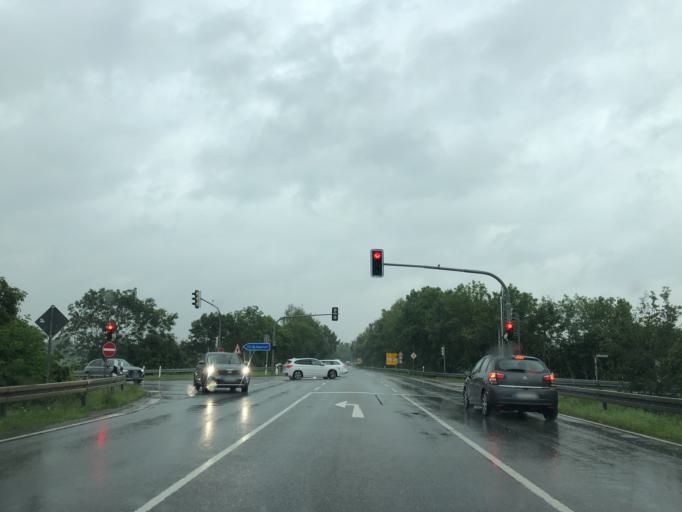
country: DE
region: Bavaria
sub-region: Upper Bavaria
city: Marzling
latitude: 48.3867
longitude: 11.7795
